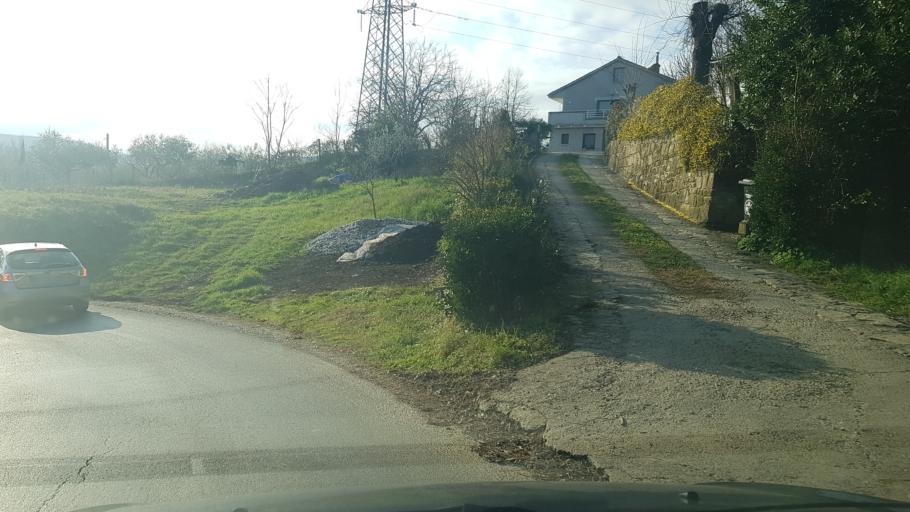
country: SI
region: Koper-Capodistria
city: Prade
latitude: 45.5326
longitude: 13.7776
